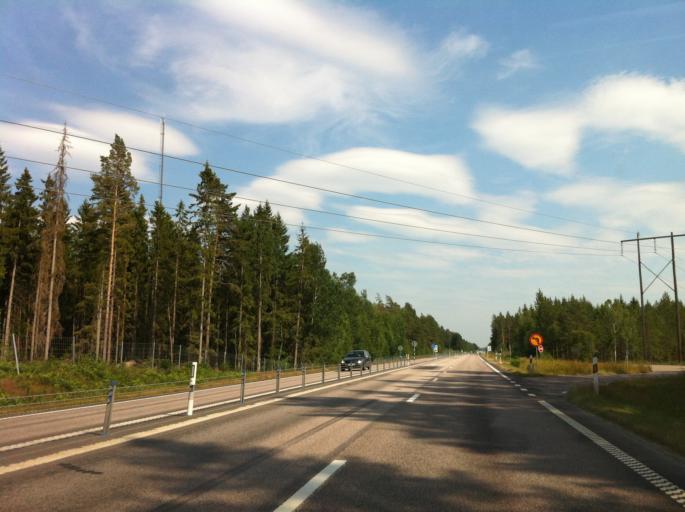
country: SE
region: Kalmar
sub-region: Kalmar Kommun
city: Trekanten
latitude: 56.7237
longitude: 16.0154
